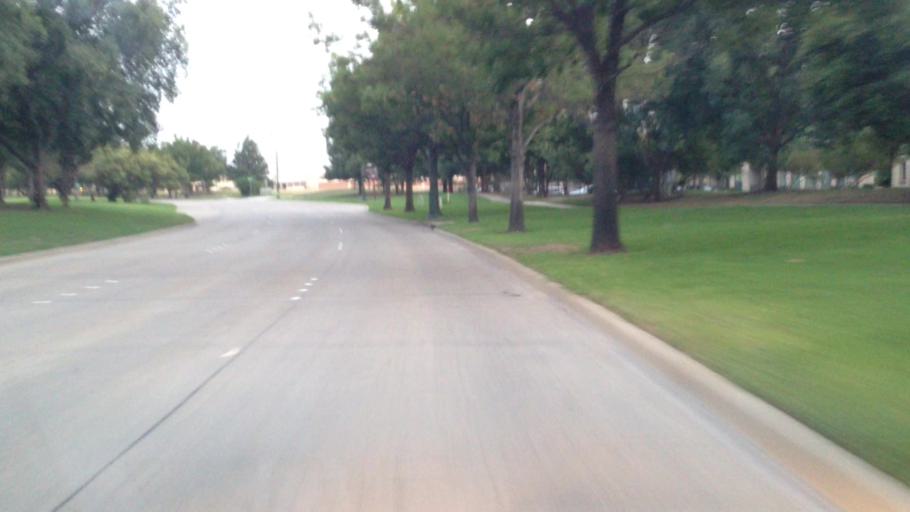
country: US
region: Texas
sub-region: Collin County
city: Frisco
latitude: 33.0982
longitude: -96.8172
